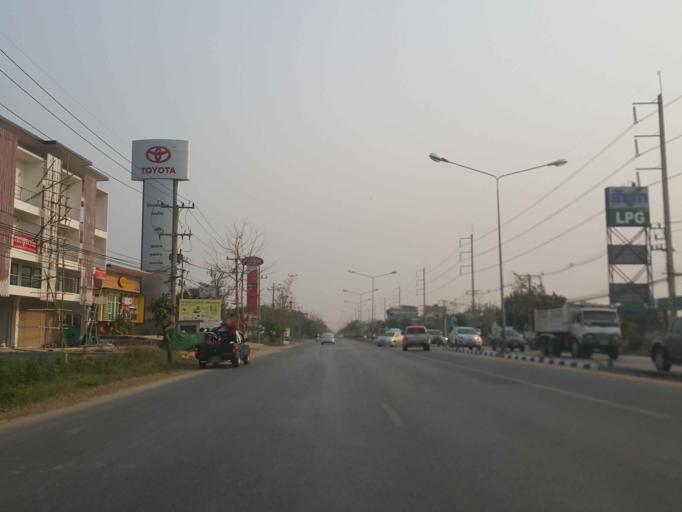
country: TH
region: Chiang Mai
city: San Sai
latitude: 18.8576
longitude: 99.0146
